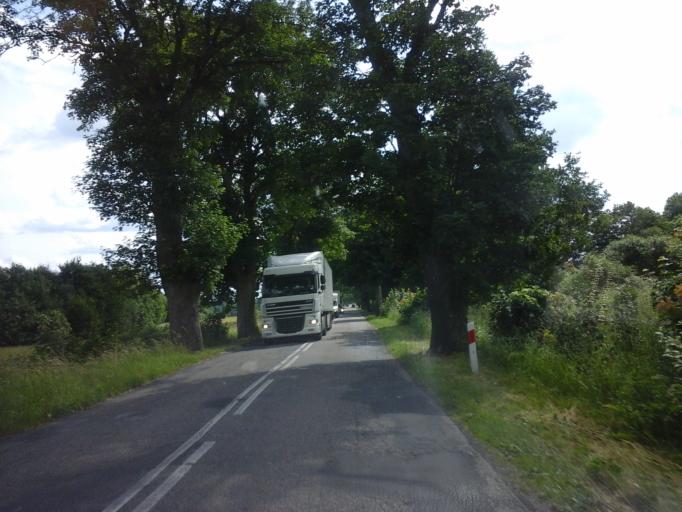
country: PL
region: West Pomeranian Voivodeship
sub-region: Powiat swidwinski
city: Swidwin
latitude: 53.7497
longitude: 15.7294
